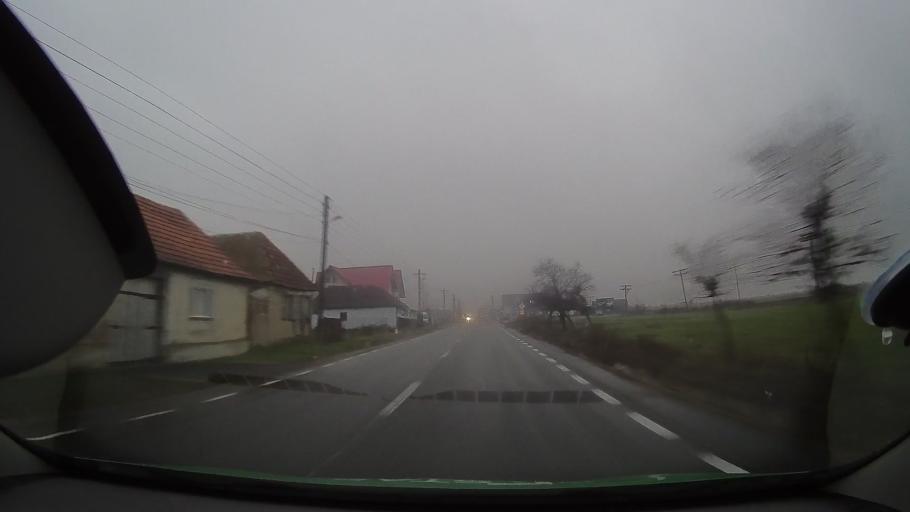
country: RO
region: Bihor
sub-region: Comuna Olcea
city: Olcea
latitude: 46.6857
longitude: 21.9661
